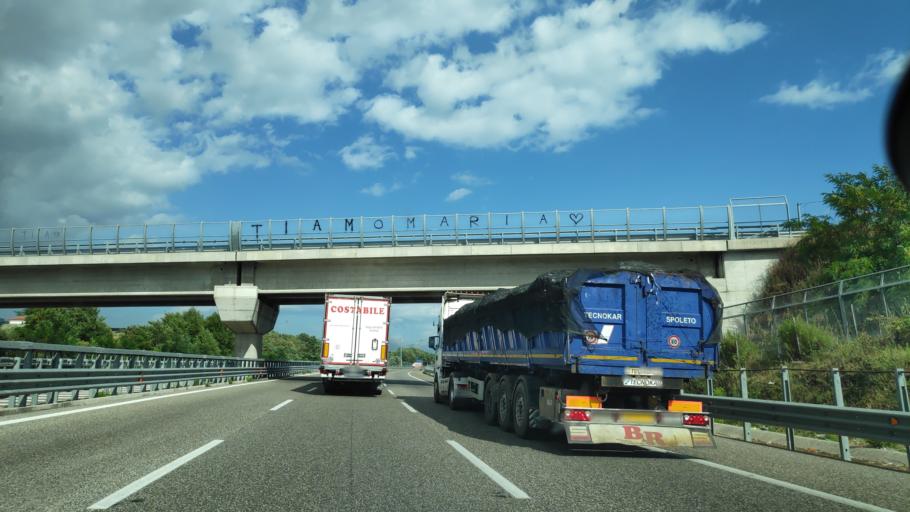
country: IT
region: Campania
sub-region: Provincia di Salerno
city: Contursi Terme
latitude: 40.6143
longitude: 15.2756
